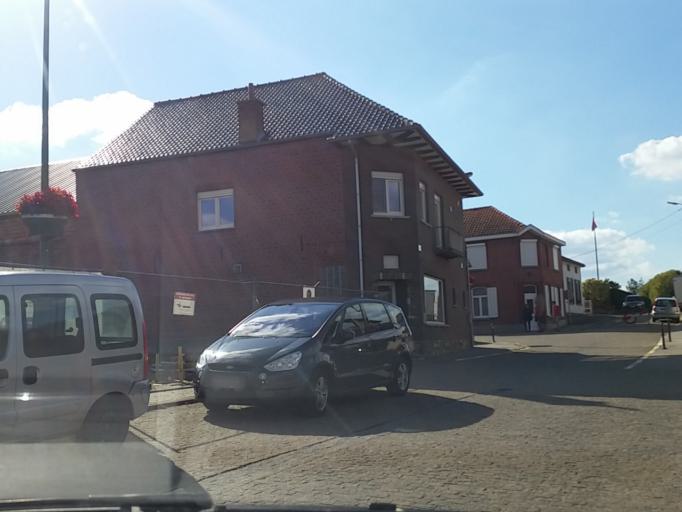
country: BE
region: Flanders
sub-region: Provincie Vlaams-Brabant
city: Holsbeek
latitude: 50.9253
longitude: 4.8066
